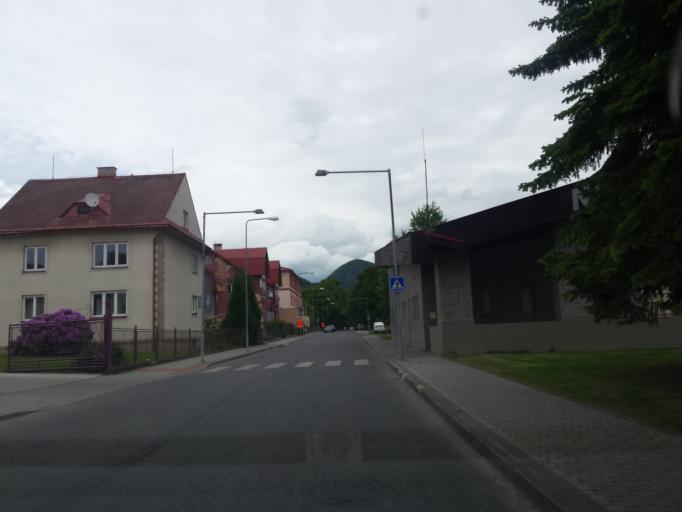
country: CZ
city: Novy Bor
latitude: 50.7637
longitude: 14.5492
